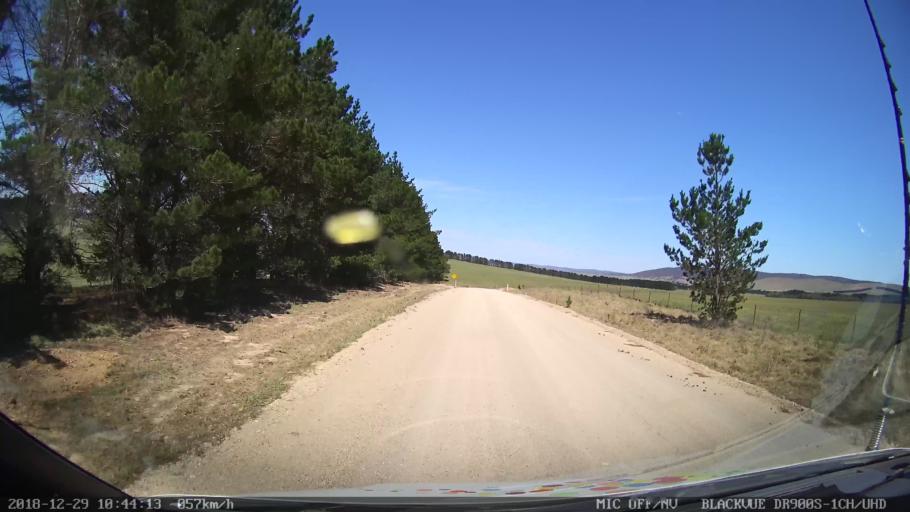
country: AU
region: New South Wales
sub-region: Palerang
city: Bungendore
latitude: -35.0414
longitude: 149.5303
